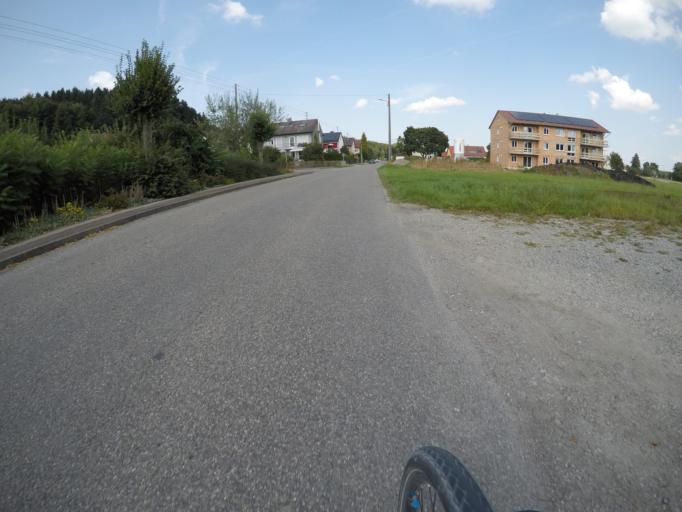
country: DE
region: Bavaria
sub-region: Swabia
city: Kuhlenthal
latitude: 48.5678
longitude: 10.8226
